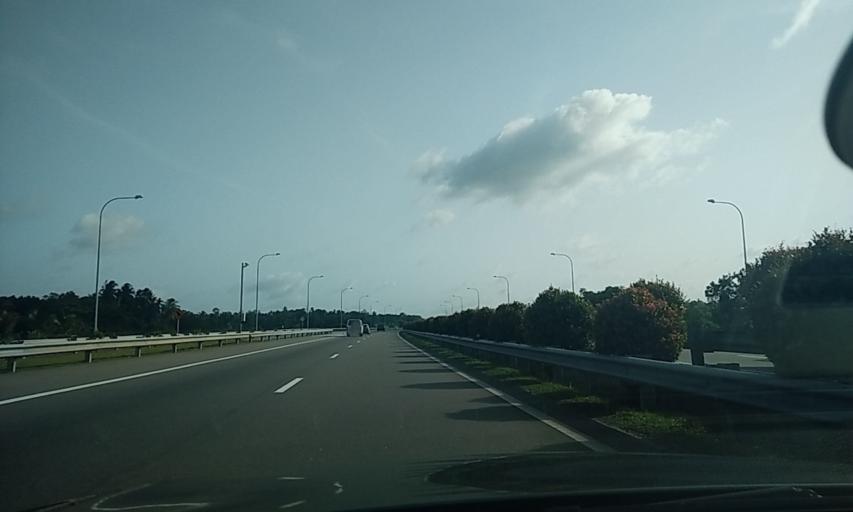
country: LK
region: Western
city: Homagama
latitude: 6.8842
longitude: 79.9765
